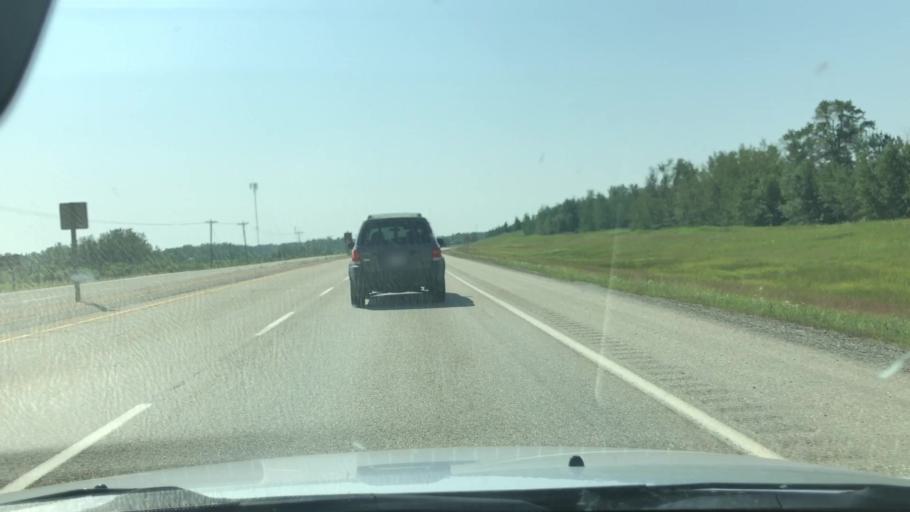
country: CA
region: Alberta
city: Devon
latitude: 53.4521
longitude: -113.7630
